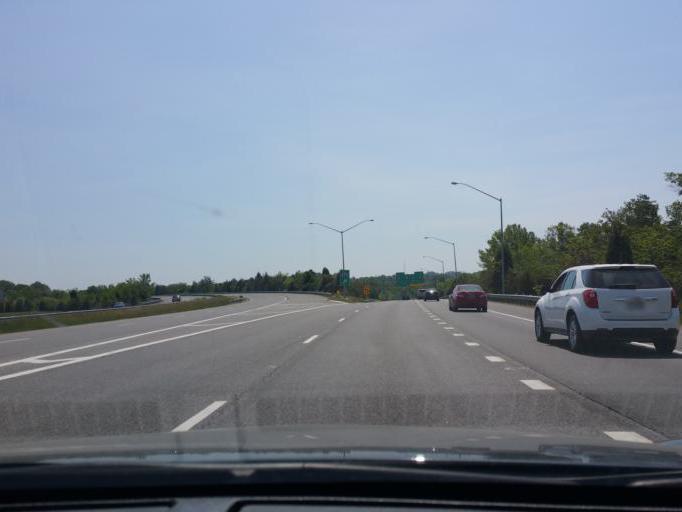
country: US
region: Maryland
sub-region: Baltimore County
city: Woodlawn
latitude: 39.3066
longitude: -76.7520
